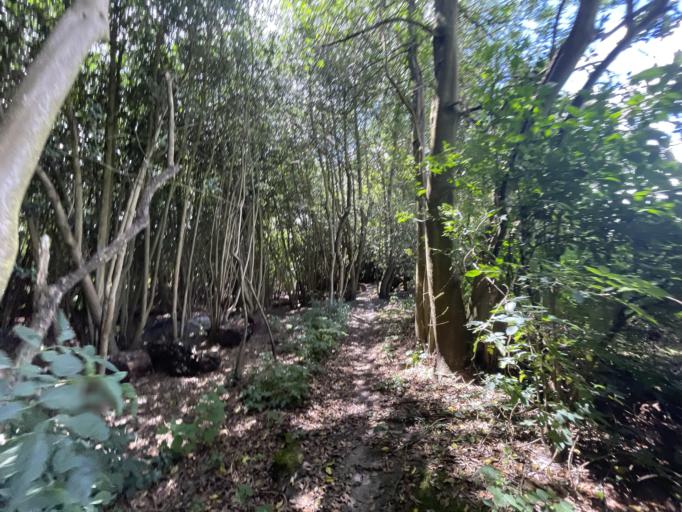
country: GB
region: England
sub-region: Kent
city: Edenbridge
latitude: 51.1630
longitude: 0.1394
